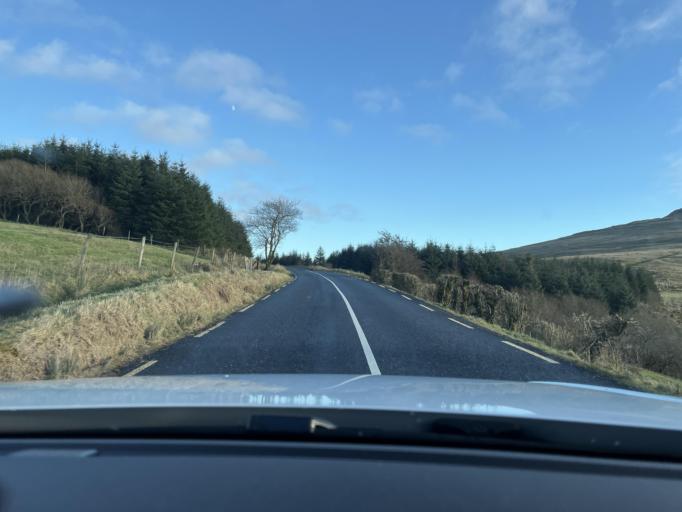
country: IE
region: Ulster
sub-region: An Cabhan
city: Ballyconnell
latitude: 54.1705
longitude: -7.8373
